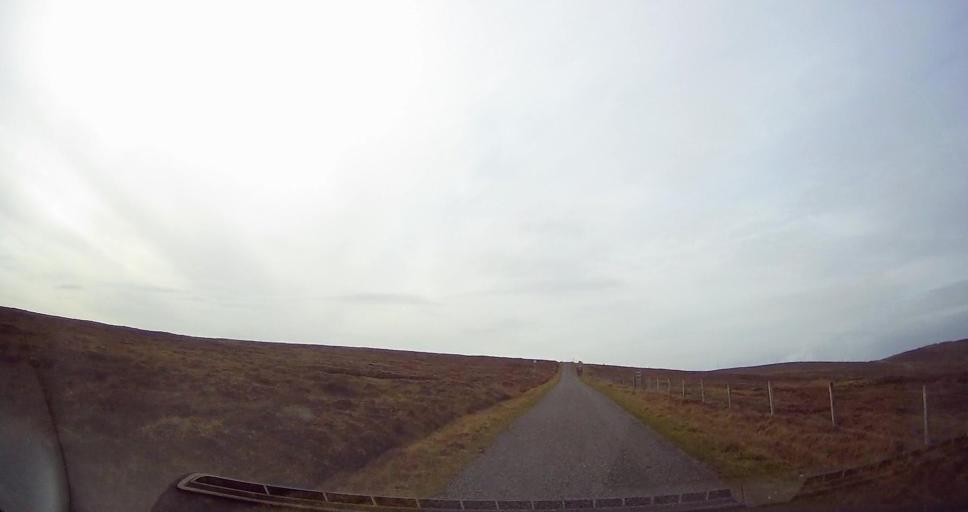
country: GB
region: Scotland
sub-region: Shetland Islands
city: Shetland
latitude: 60.1512
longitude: -1.0858
